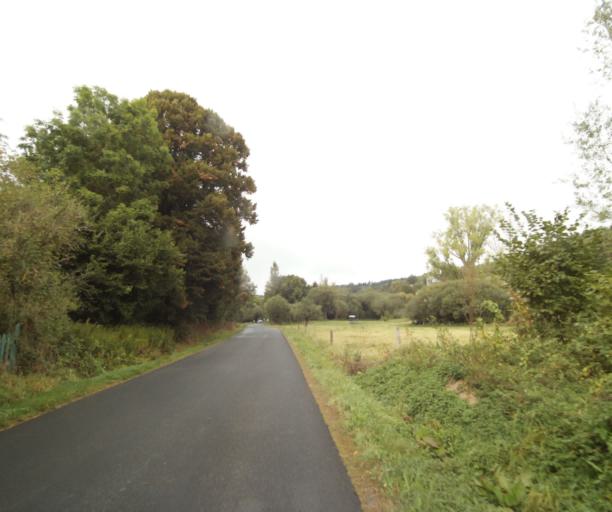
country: FR
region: Auvergne
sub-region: Departement du Puy-de-Dome
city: Saint-Genes-Champanelle
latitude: 45.7238
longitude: 2.9915
